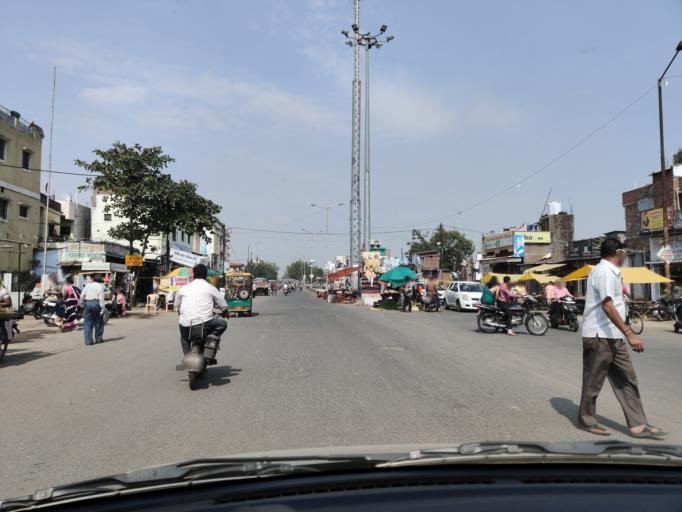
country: IN
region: Maharashtra
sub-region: Nagpur Division
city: Nagpur
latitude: 21.1603
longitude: 79.1163
